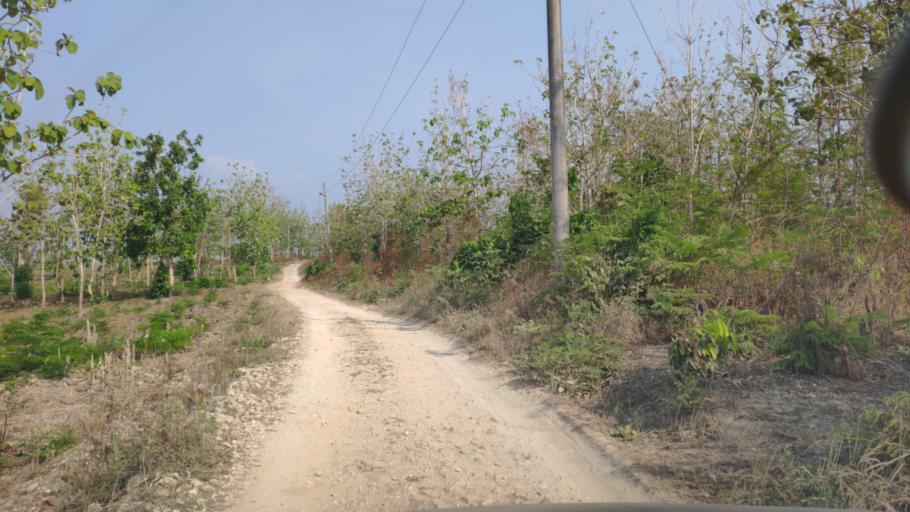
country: ID
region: Central Java
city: Jomblang
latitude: -7.0288
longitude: 111.4583
